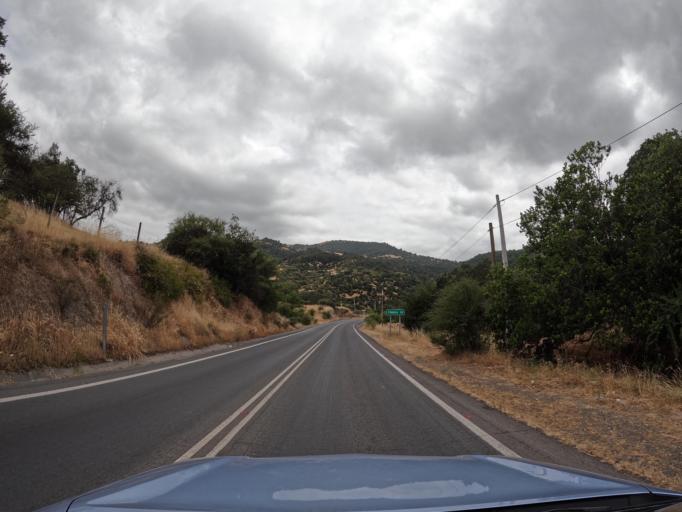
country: CL
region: Maule
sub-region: Provincia de Curico
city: Teno
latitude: -34.8168
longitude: -71.2021
